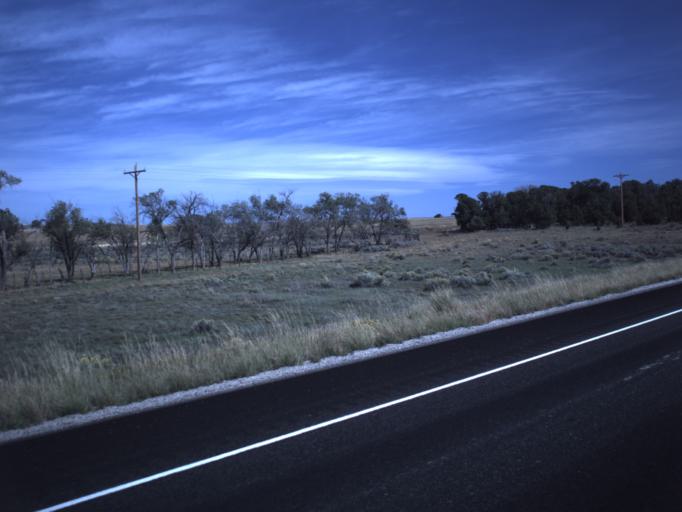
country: US
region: Utah
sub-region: San Juan County
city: Monticello
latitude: 37.8582
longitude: -109.1997
